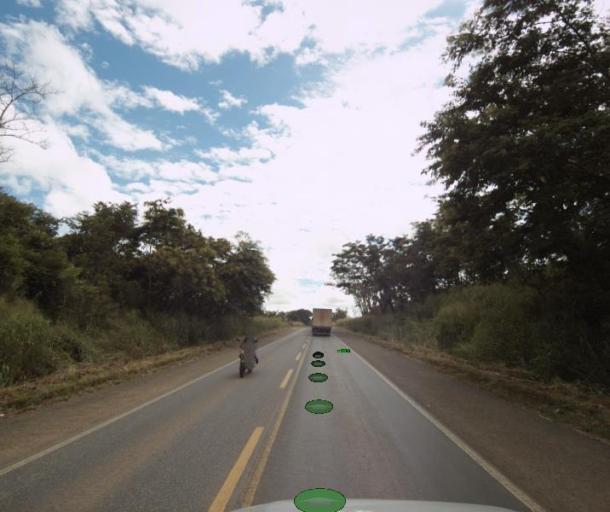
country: BR
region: Goias
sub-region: Uruacu
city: Uruacu
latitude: -14.4115
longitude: -49.1573
